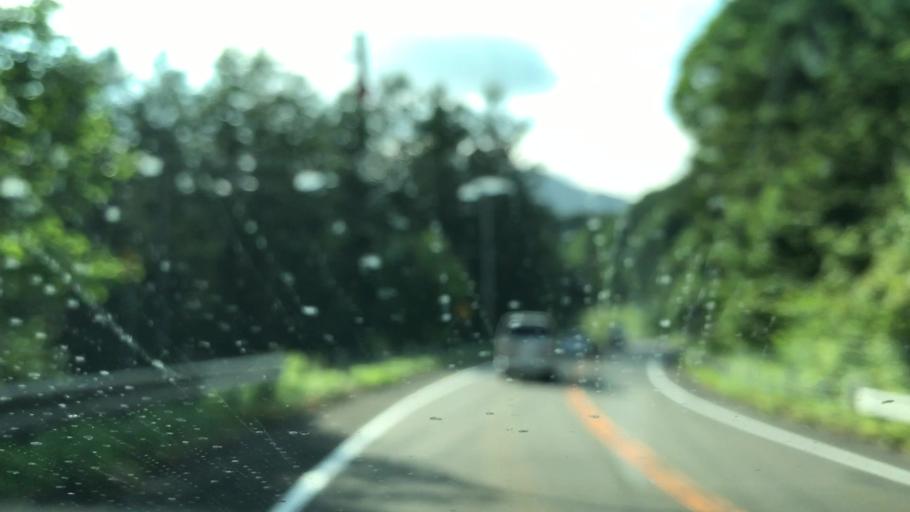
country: JP
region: Hokkaido
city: Shimo-furano
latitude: 42.8911
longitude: 142.1931
